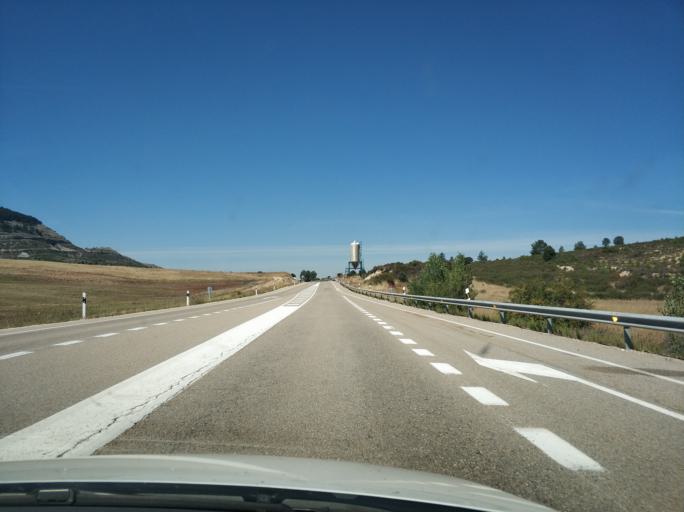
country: ES
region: Castille and Leon
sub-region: Provincia de Burgos
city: Mambrillas de Lara
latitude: 42.0992
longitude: -3.4943
